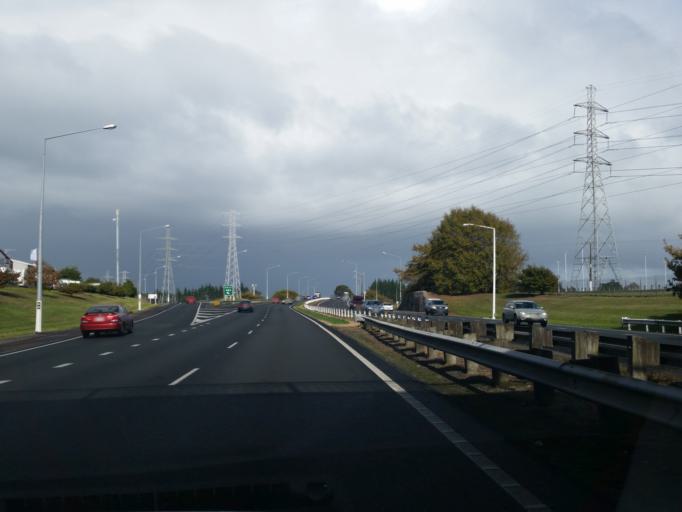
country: NZ
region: Auckland
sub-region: Auckland
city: Papakura
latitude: -37.1036
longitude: 174.9455
